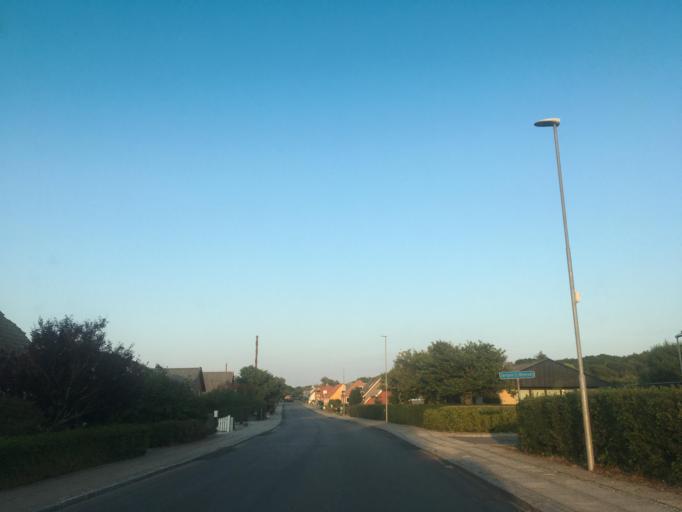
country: DK
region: North Denmark
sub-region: Thisted Kommune
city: Hurup
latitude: 56.7639
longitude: 8.3103
